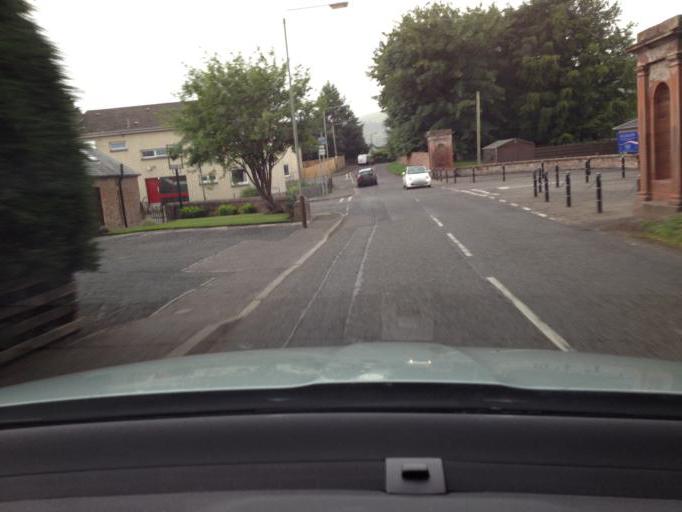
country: GB
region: Scotland
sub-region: Perth and Kinross
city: Bridge of Earn
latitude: 56.3415
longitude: -3.4098
